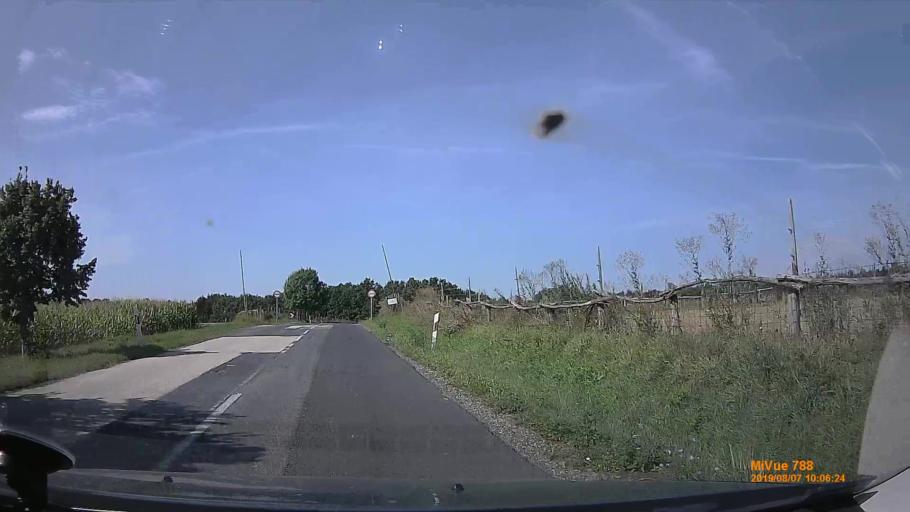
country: HU
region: Zala
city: Zalaegerszeg
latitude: 46.6920
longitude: 16.7403
